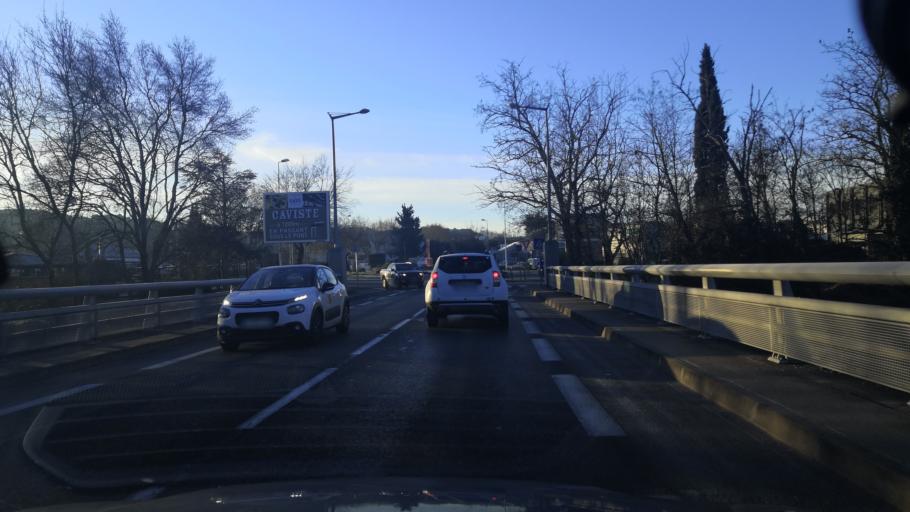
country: FR
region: Provence-Alpes-Cote d'Azur
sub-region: Departement des Bouches-du-Rhone
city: Aix-en-Provence
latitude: 43.5089
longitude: 5.4088
